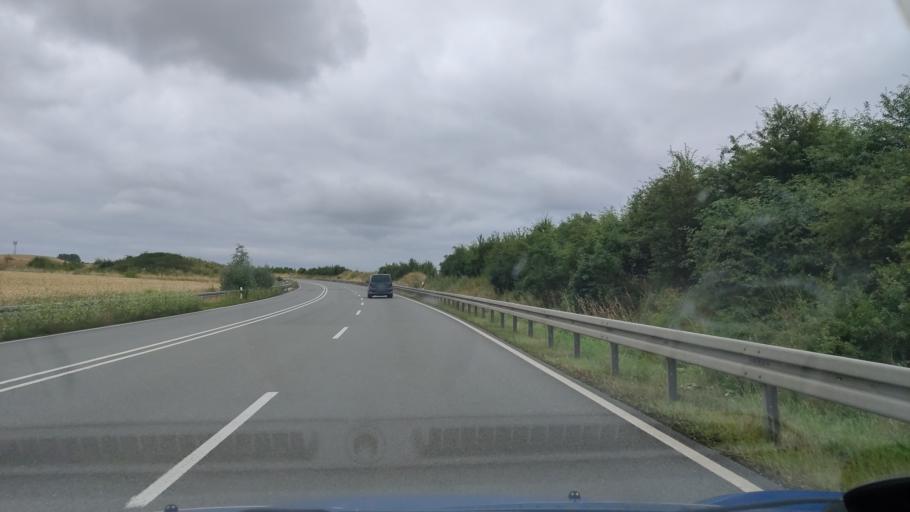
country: DE
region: Lower Saxony
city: Messenkamp
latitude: 52.2362
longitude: 9.3996
